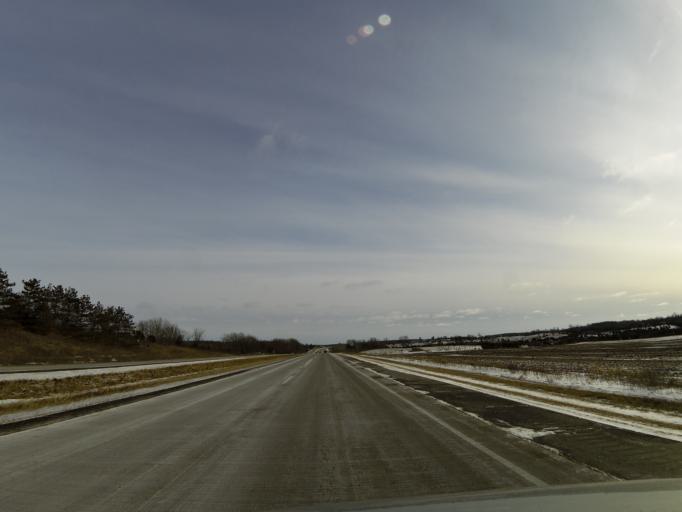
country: US
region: Wisconsin
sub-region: Pierce County
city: River Falls
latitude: 44.9247
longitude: -92.6776
